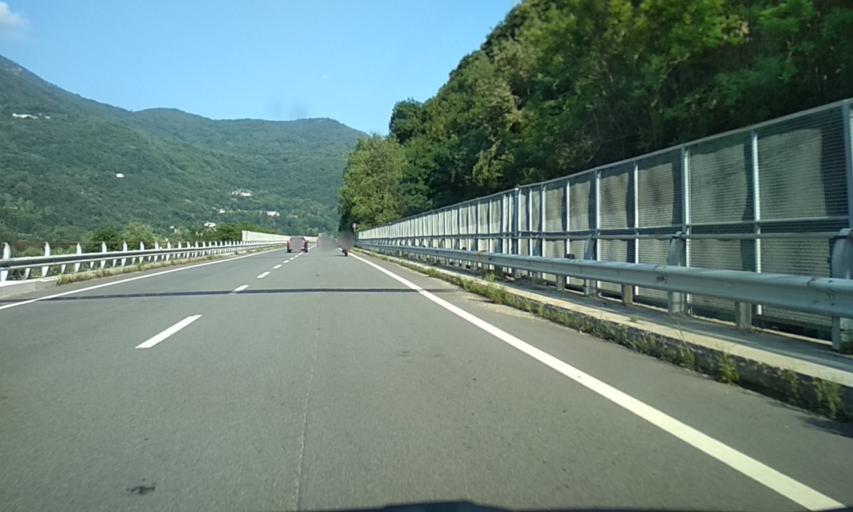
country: IT
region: Piedmont
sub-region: Provincia di Torino
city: Pont-Canavese
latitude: 45.4178
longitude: 7.5970
